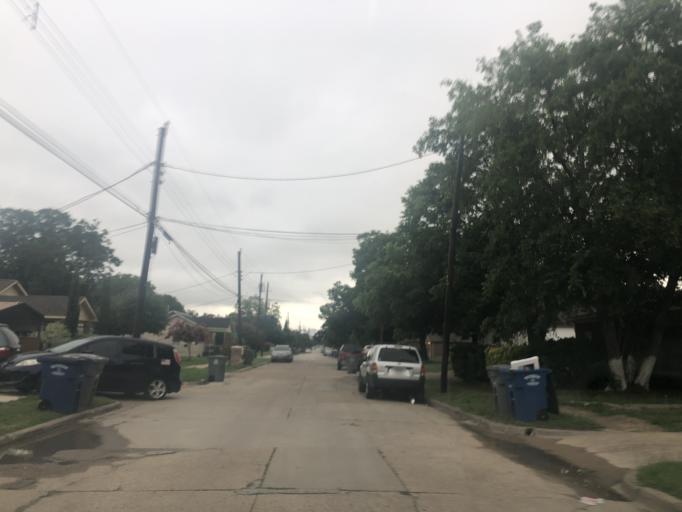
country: US
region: Texas
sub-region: Dallas County
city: Cockrell Hill
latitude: 32.7818
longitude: -96.8816
